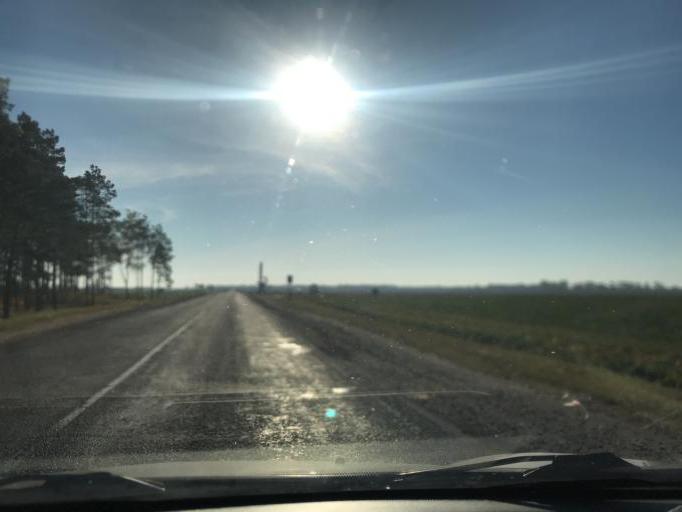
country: BY
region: Gomel
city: Khoyniki
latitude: 51.8125
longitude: 30.1000
